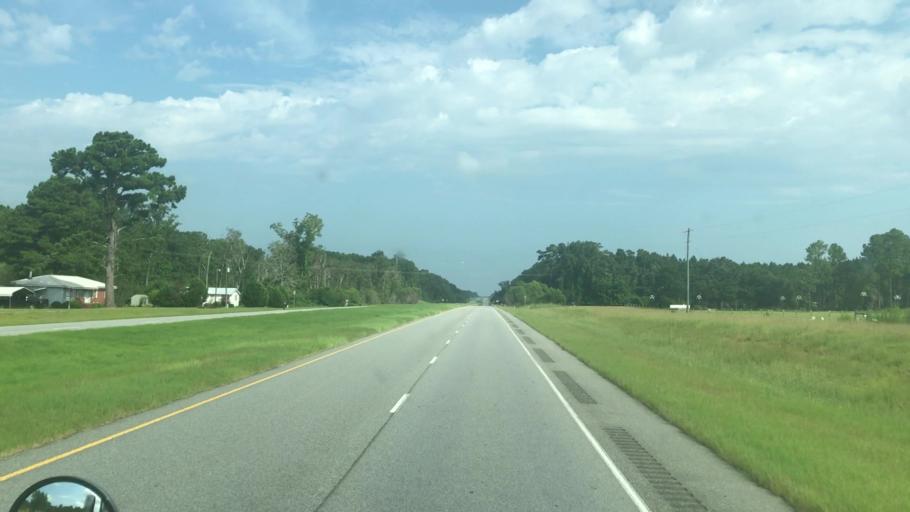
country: US
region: Georgia
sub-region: Early County
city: Blakely
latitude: 31.2927
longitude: -84.8510
